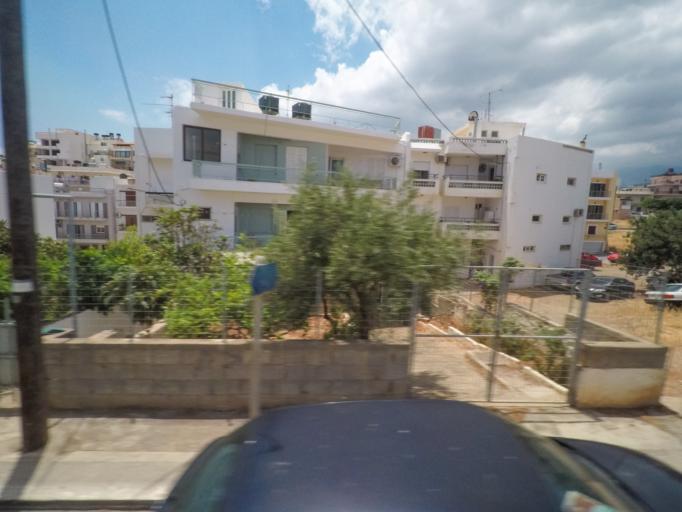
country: GR
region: Crete
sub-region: Nomos Lasithiou
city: Agios Nikolaos
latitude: 35.1937
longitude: 25.7150
